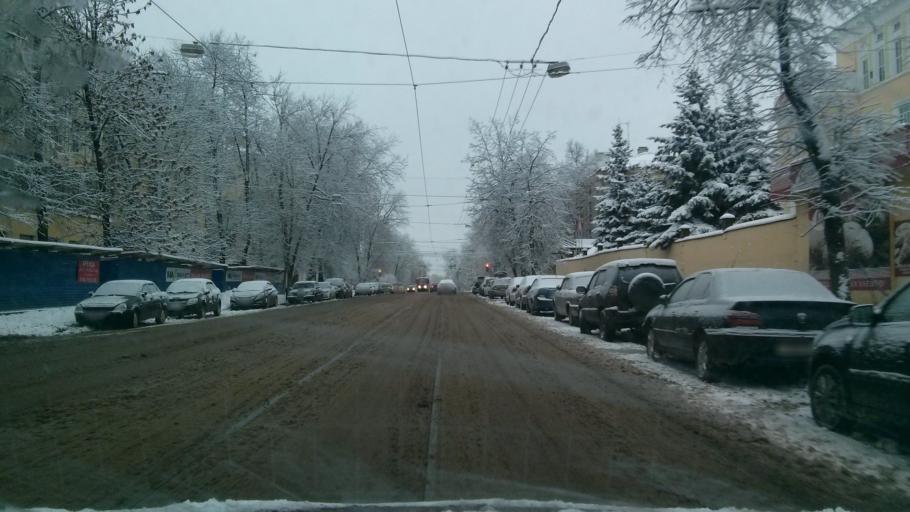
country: RU
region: Nizjnij Novgorod
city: Nizhniy Novgorod
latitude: 56.3108
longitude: 44.0167
